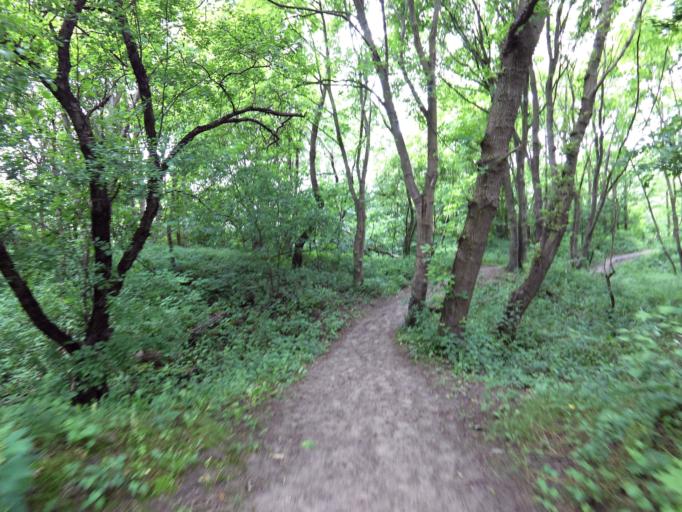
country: NL
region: South Holland
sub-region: Gemeente Hellevoetsluis
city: Nieuw-Helvoet
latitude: 51.8688
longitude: 4.0533
